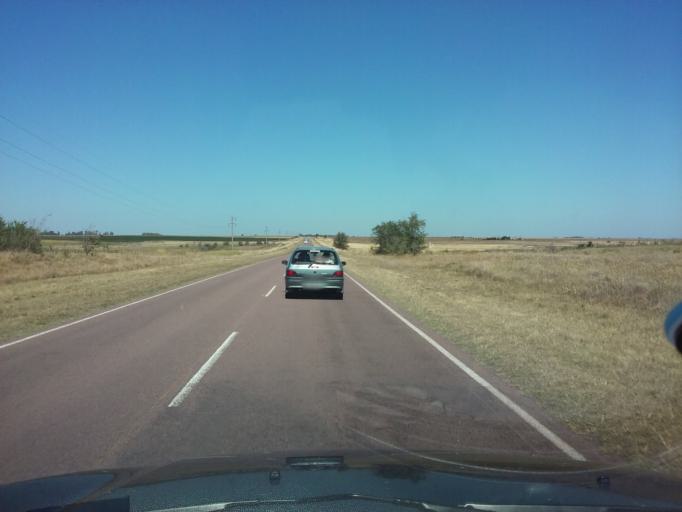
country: AR
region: La Pampa
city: Colonia Baron
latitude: -36.2067
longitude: -63.9433
